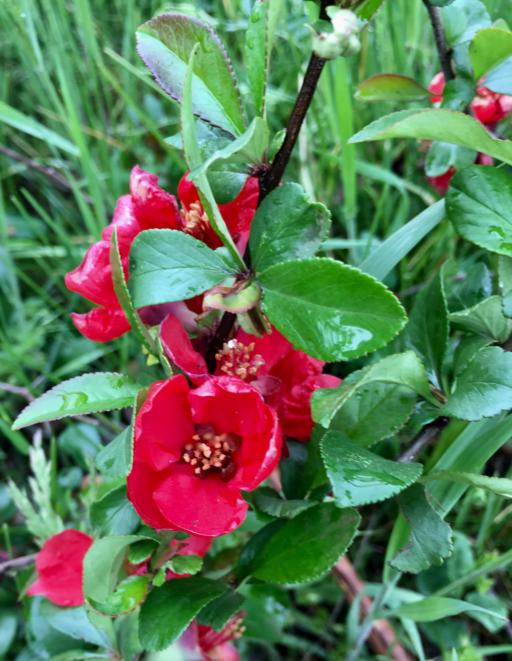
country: XK
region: Pristina
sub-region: Komuna e Drenasit
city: Glogovac
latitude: 42.6412
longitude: 20.9057
